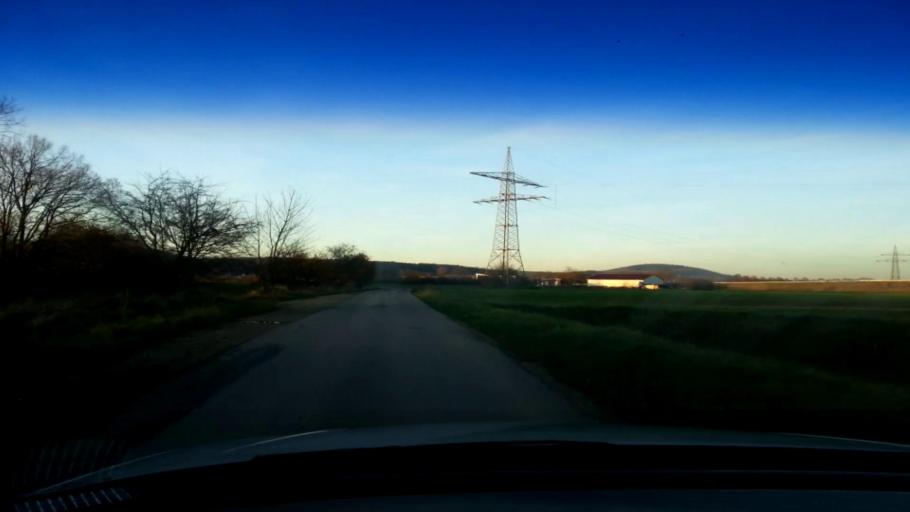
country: DE
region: Bavaria
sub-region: Upper Franconia
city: Ebensfeld
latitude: 50.0568
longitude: 10.9498
